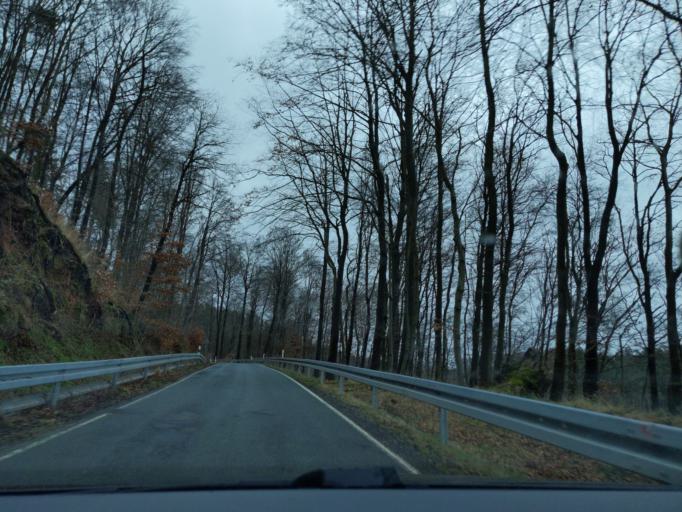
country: DE
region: Hesse
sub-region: Regierungsbezirk Kassel
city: Bad Arolsen
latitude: 51.3244
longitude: 9.0229
